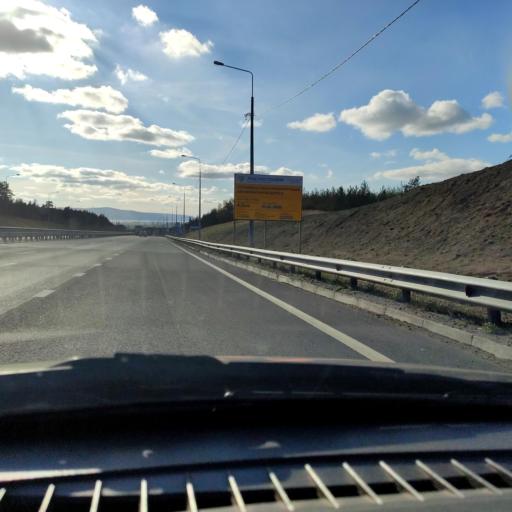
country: RU
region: Samara
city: Zhigulevsk
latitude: 53.4970
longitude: 49.5359
